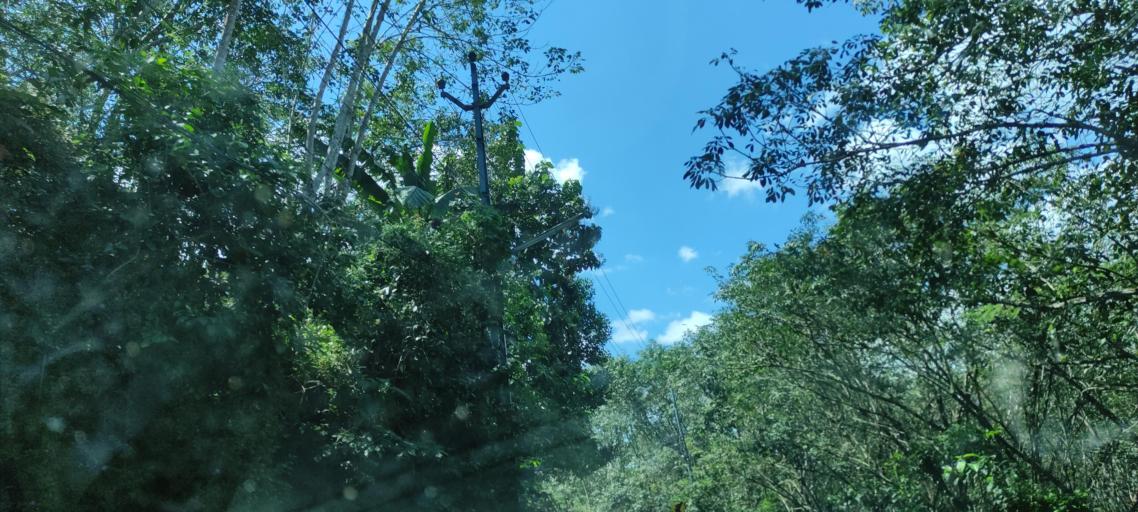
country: IN
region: Kerala
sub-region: Pattanamtitta
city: Adur
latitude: 9.1267
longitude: 76.7041
